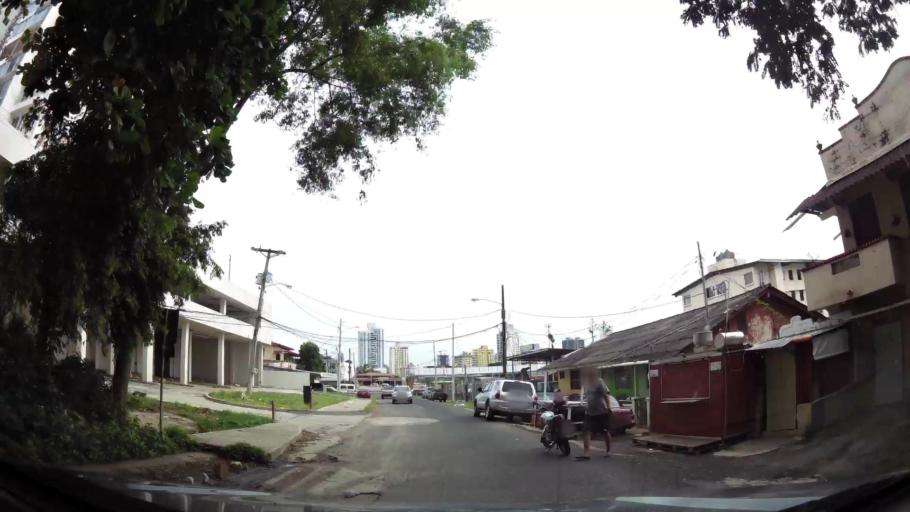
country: PA
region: Panama
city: Panama
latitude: 9.0091
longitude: -79.5197
